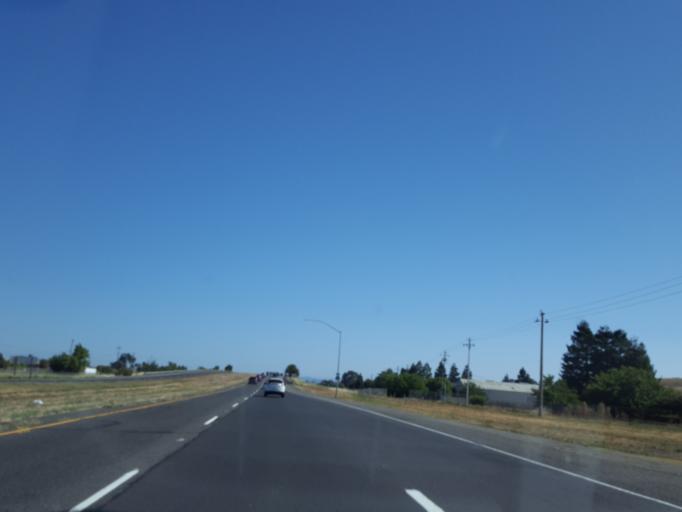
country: US
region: California
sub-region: Napa County
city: American Canyon
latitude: 38.1955
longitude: -122.2563
